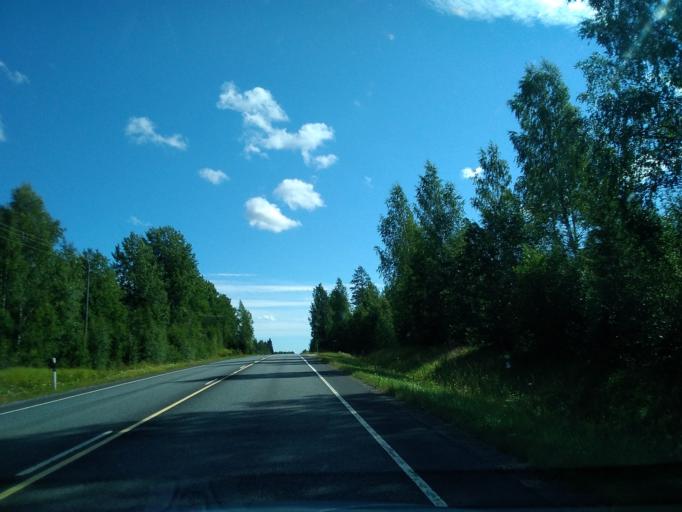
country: FI
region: Haeme
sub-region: Haemeenlinna
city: Renko
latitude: 60.8354
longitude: 24.0742
